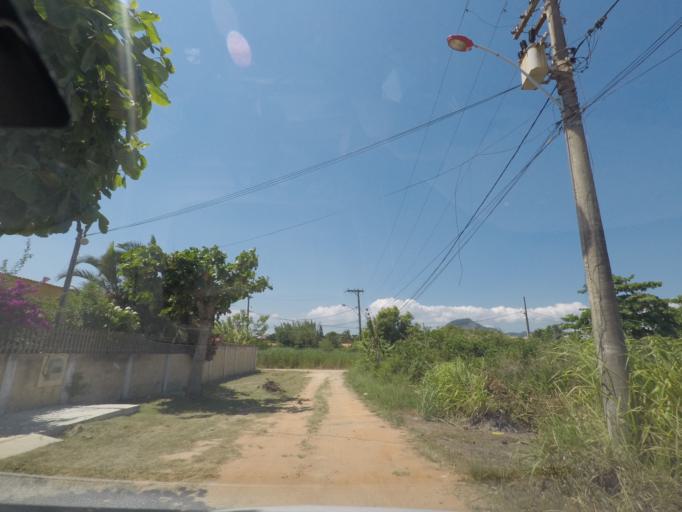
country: BR
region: Rio de Janeiro
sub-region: Marica
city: Marica
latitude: -22.9722
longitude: -42.9316
